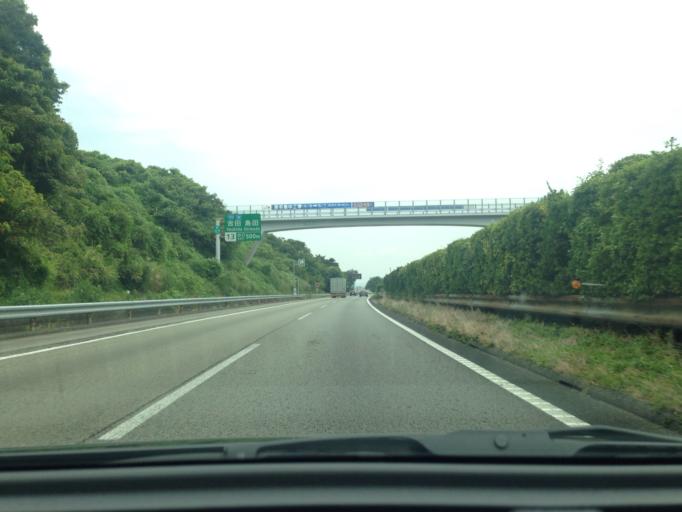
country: JP
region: Shizuoka
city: Shimada
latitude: 34.7841
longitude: 138.2300
